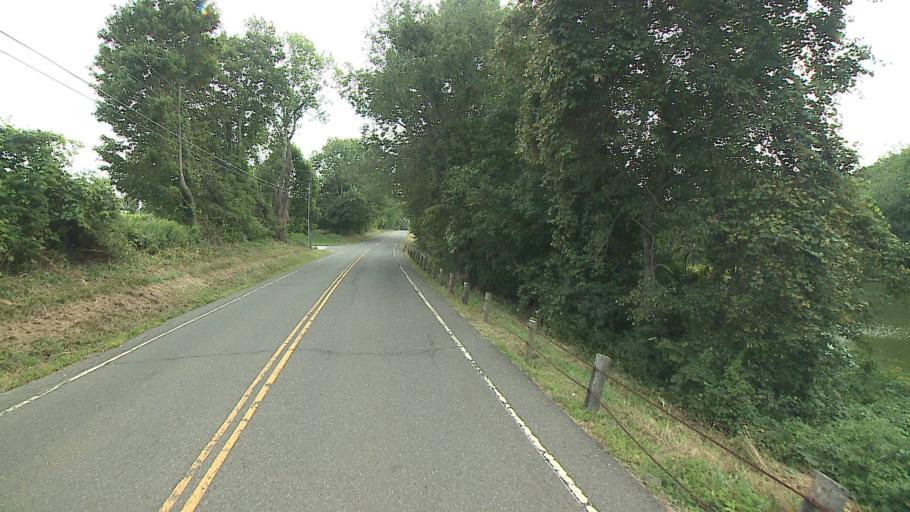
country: US
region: Connecticut
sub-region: Litchfield County
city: Bethlehem Village
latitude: 41.6466
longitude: -73.1958
